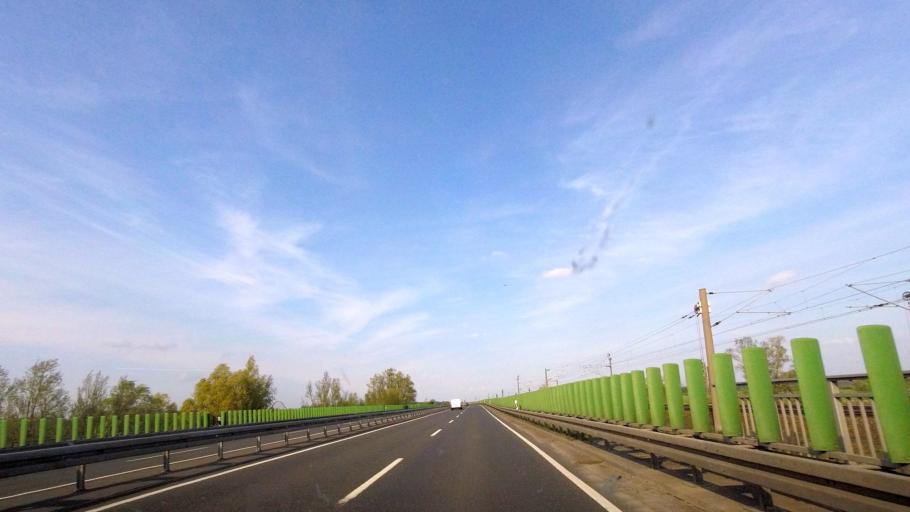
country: DE
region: Saxony-Anhalt
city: Wittenburg
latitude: 51.8464
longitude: 12.6426
